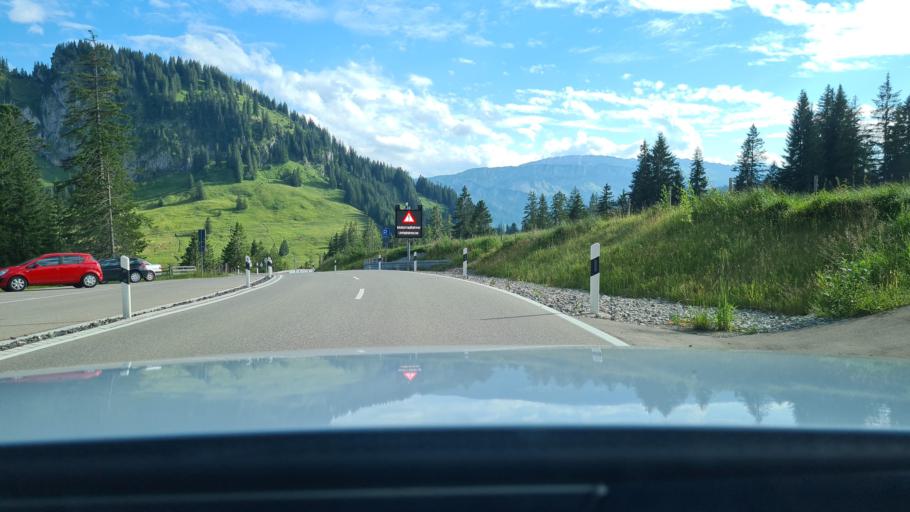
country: DE
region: Bavaria
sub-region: Swabia
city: Obermaiselstein
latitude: 47.4362
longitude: 10.1733
